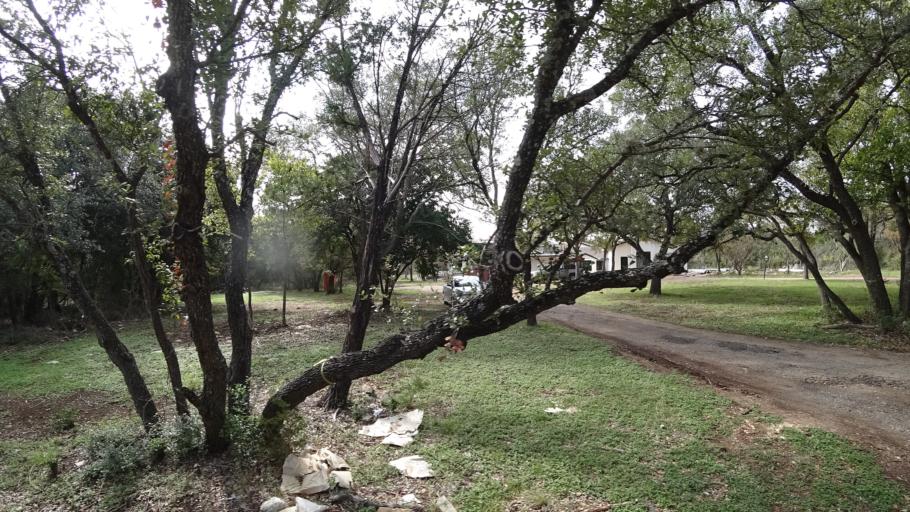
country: US
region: Texas
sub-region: Travis County
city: Wells Branch
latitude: 30.4294
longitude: -97.7046
